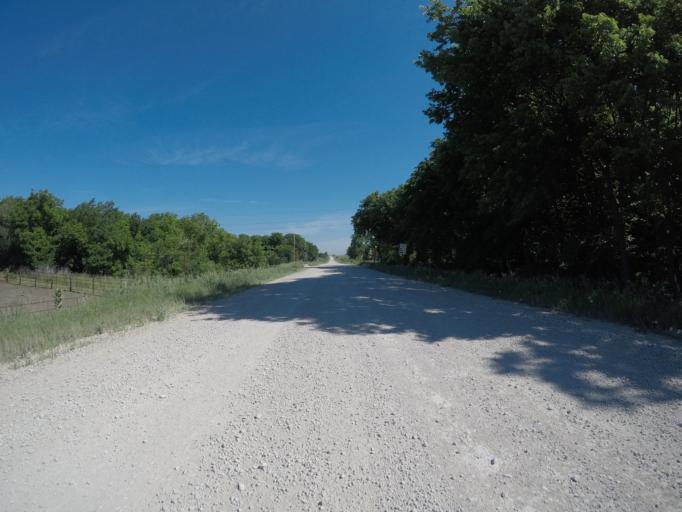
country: US
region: Kansas
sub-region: Wabaunsee County
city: Alma
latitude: 38.9922
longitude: -96.1138
